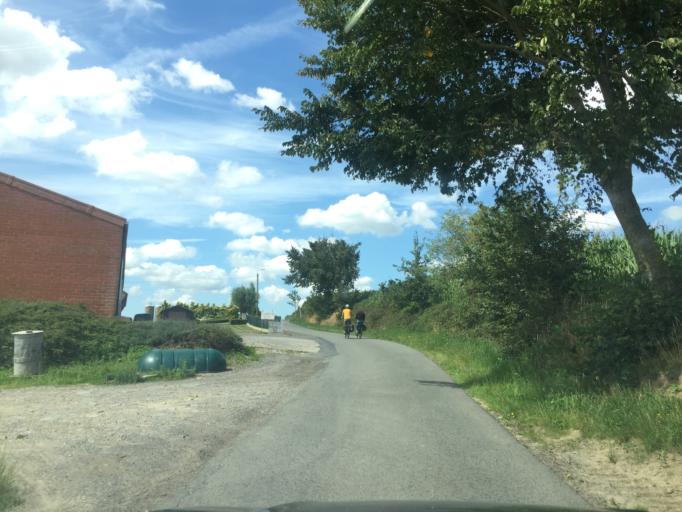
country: BE
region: Flanders
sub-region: Provincie West-Vlaanderen
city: Staden
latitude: 50.9446
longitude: 3.0114
